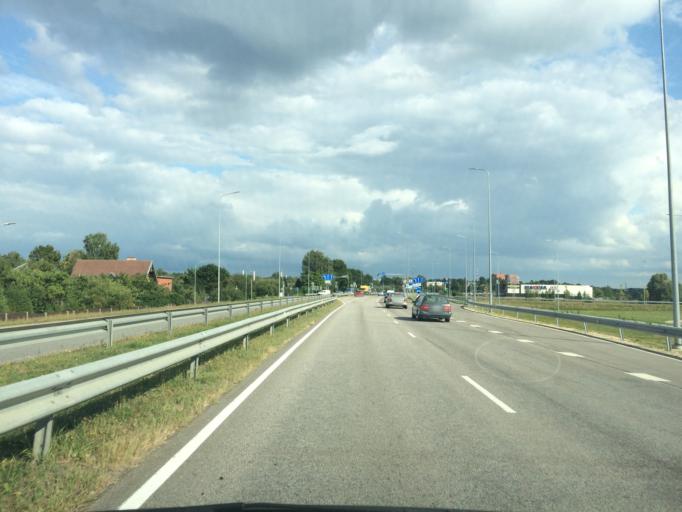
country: LV
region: Ogre
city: Ogre
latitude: 56.8183
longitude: 24.5773
